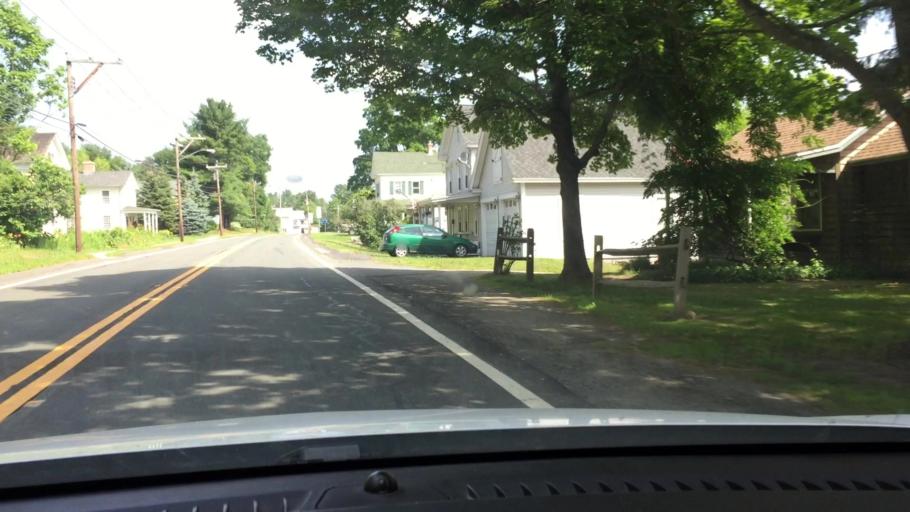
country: US
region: Massachusetts
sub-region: Berkshire County
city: Otis
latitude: 42.1902
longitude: -73.0909
